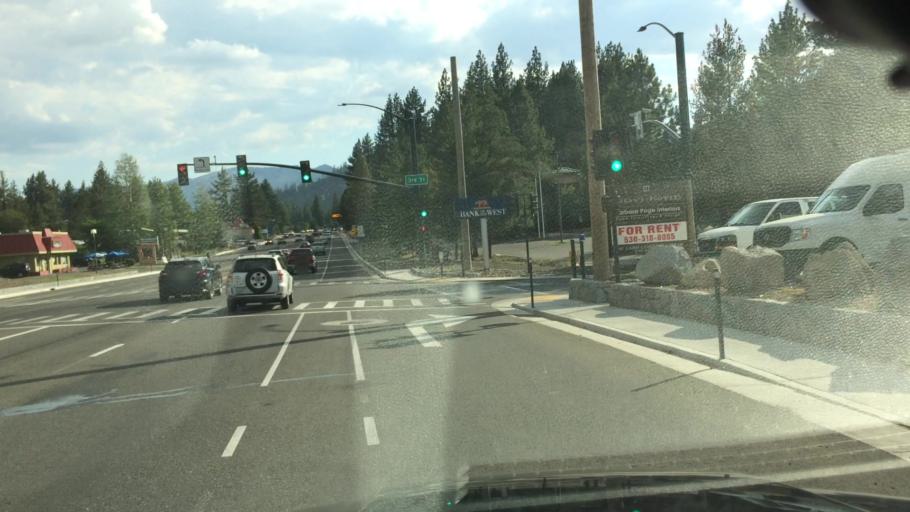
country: US
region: California
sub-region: El Dorado County
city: South Lake Tahoe
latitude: 38.9171
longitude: -119.9988
